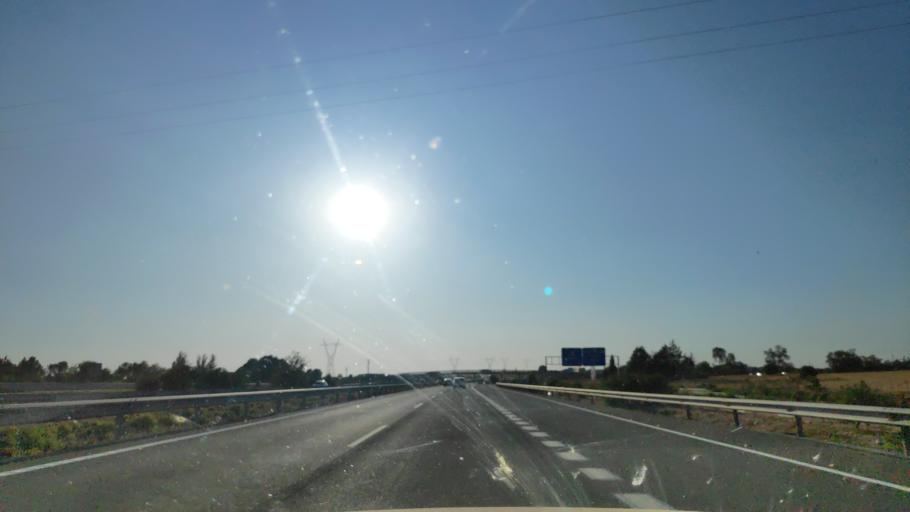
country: ES
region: Castille-La Mancha
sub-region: Provincia de Cuenca
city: Tarancon
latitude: 39.9959
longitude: -3.0124
